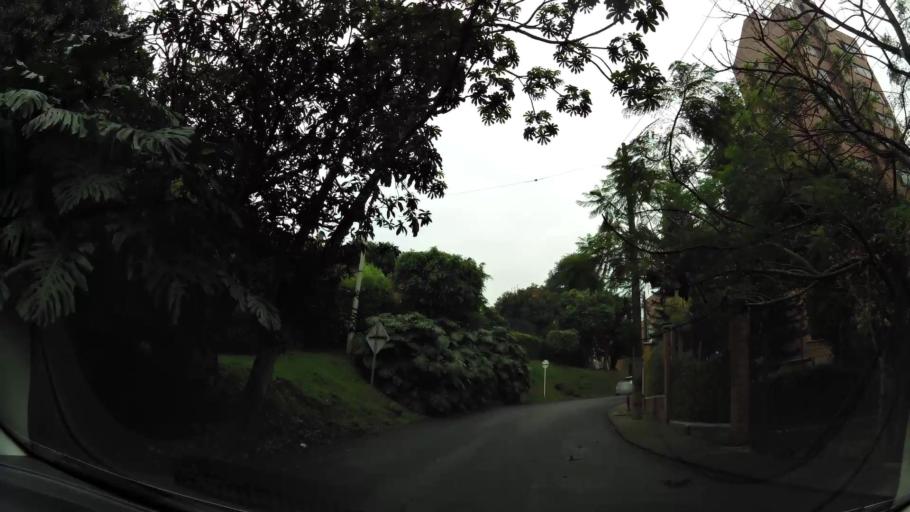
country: CO
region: Antioquia
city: Envigado
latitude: 6.1924
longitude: -75.5657
